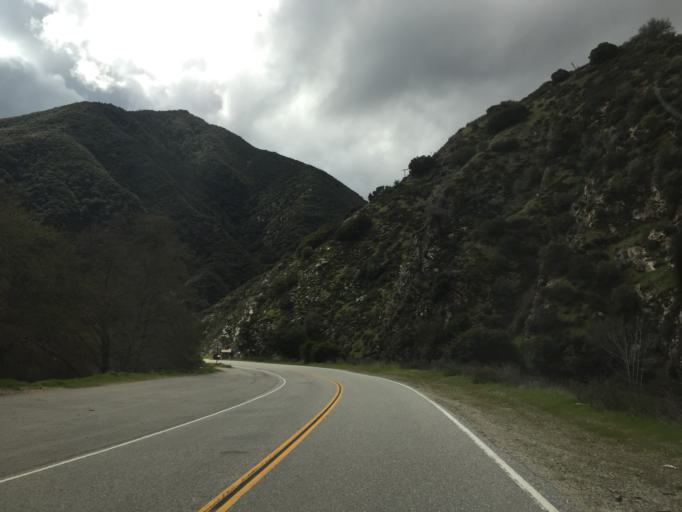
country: US
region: California
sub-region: Los Angeles County
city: Glendora
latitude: 34.2454
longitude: -117.8686
